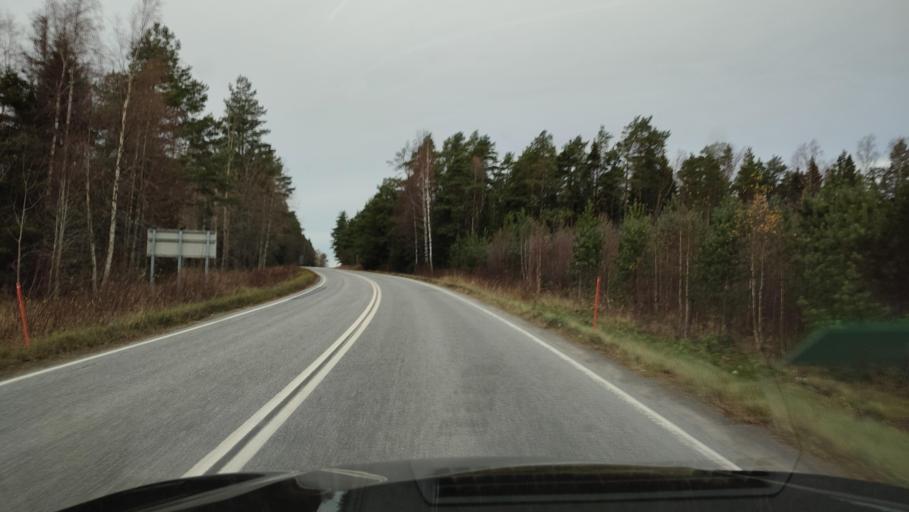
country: FI
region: Ostrobothnia
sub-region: Sydosterbotten
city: Naerpes
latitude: 62.4005
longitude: 21.3630
